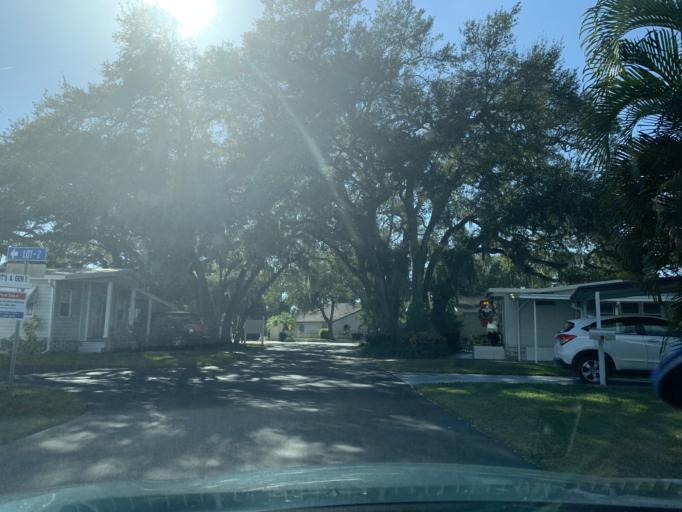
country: US
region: Florida
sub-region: Pinellas County
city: Belleair
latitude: 27.9260
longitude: -82.7943
